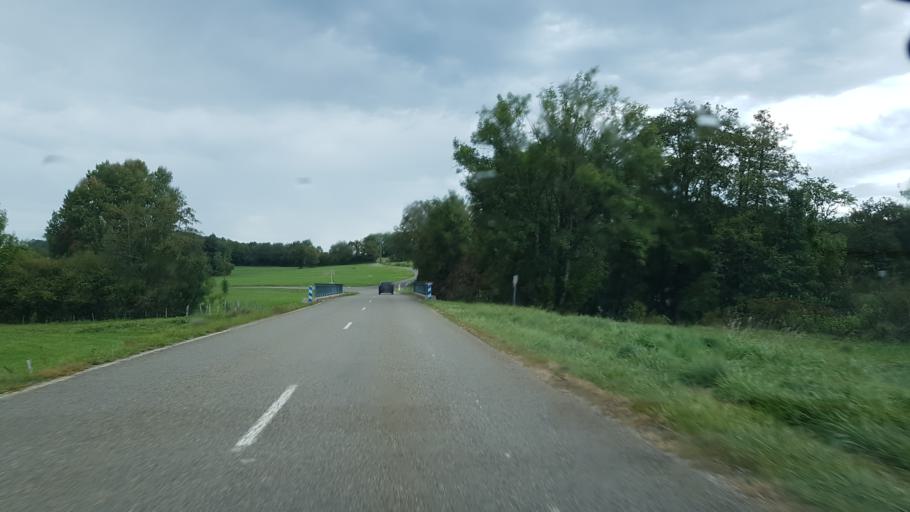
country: FR
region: Rhone-Alpes
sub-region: Departement de l'Ain
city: Cuisiat
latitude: 46.3380
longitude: 5.4377
